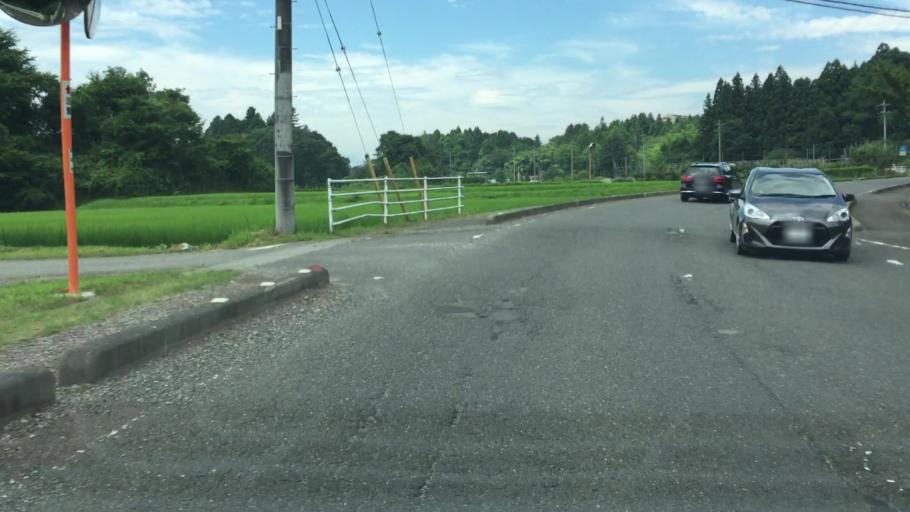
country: JP
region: Tochigi
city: Kuroiso
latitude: 37.0611
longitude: 140.0397
